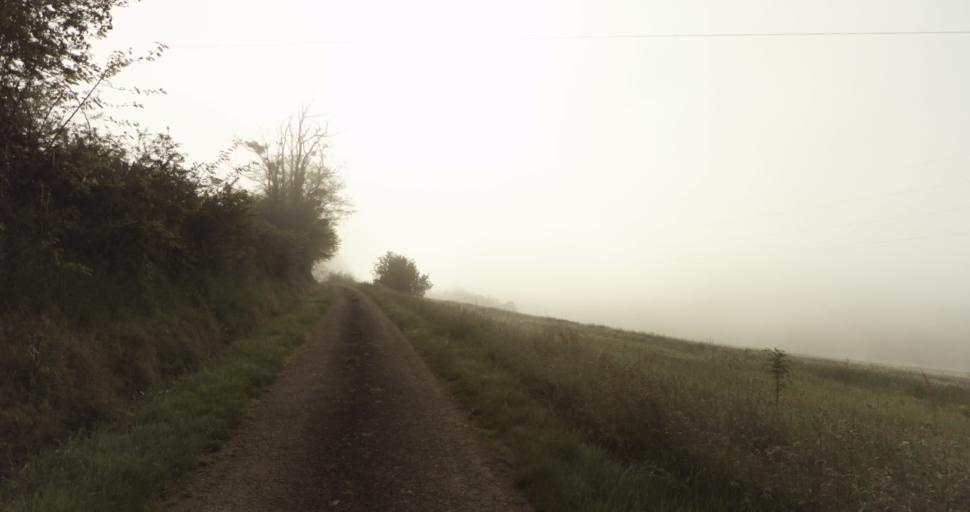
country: FR
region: Limousin
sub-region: Departement de la Haute-Vienne
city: Le Vigen
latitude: 45.7599
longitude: 1.2908
